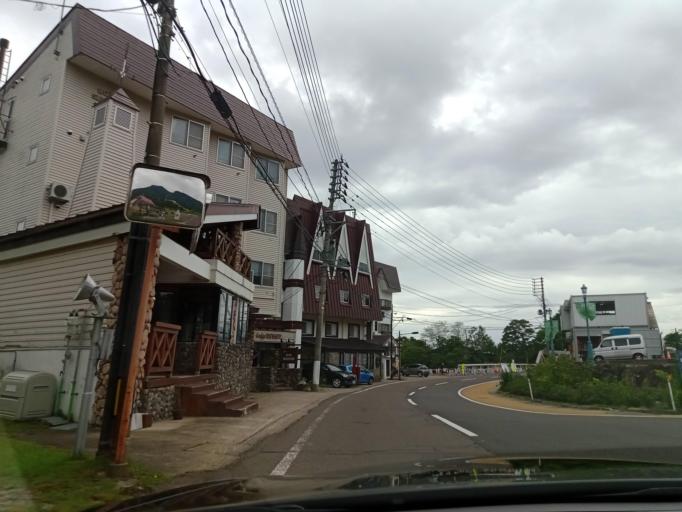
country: JP
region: Niigata
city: Arai
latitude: 36.8866
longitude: 138.1789
